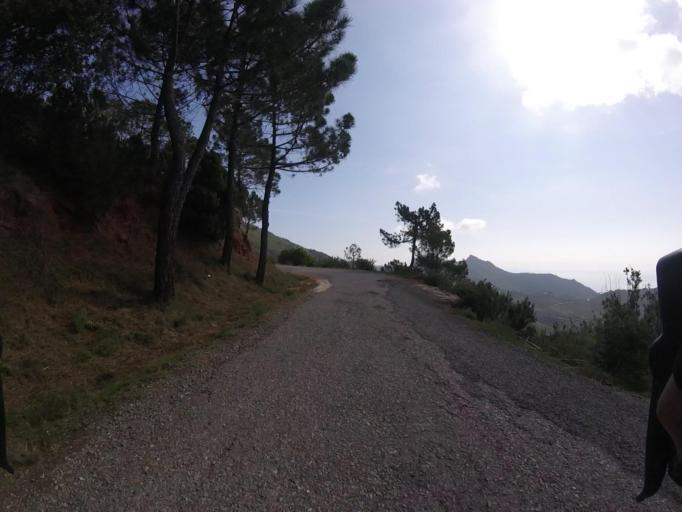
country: ES
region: Valencia
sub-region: Provincia de Castello
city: Benicassim
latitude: 40.0778
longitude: 0.0274
